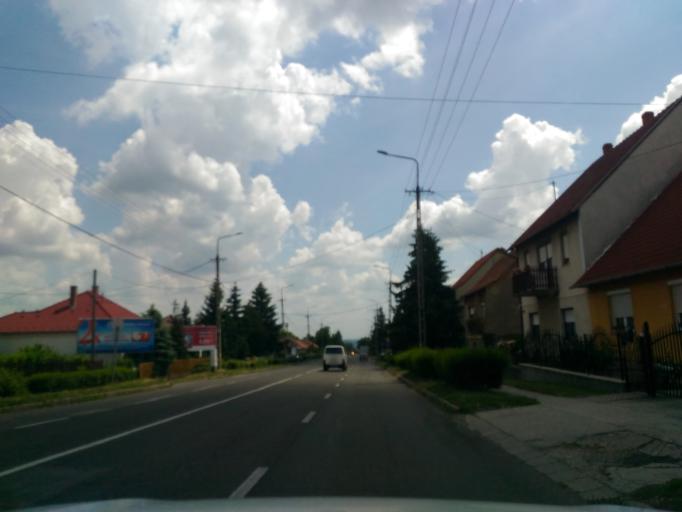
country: HU
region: Baranya
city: Pecs
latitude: 46.1108
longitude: 18.2623
